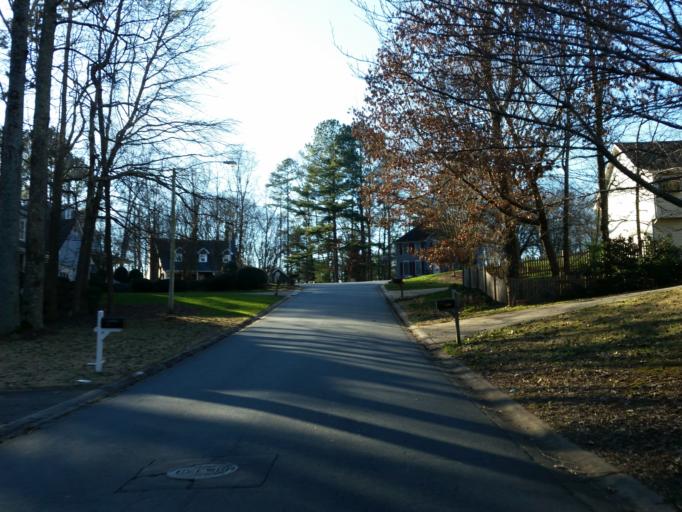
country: US
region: Georgia
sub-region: Cherokee County
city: Woodstock
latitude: 34.0529
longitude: -84.4745
